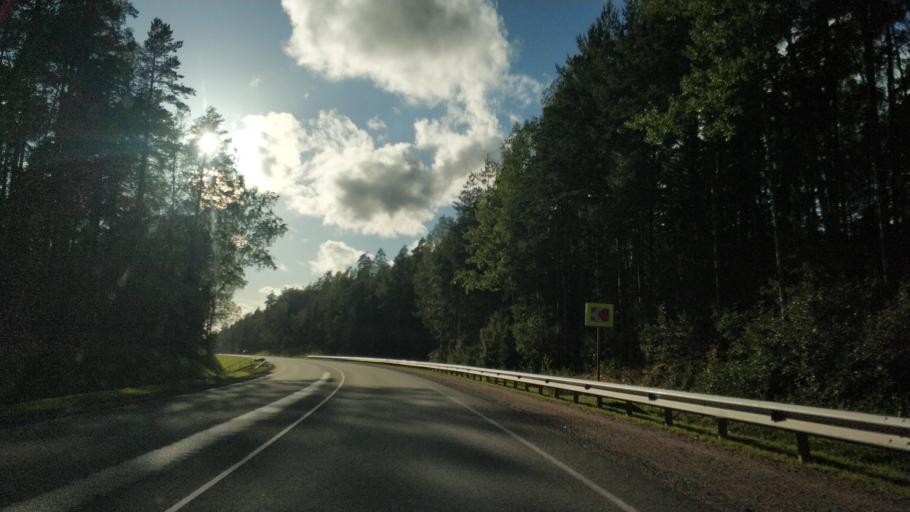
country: RU
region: Leningrad
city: Sapernoye
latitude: 60.7158
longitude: 30.0089
